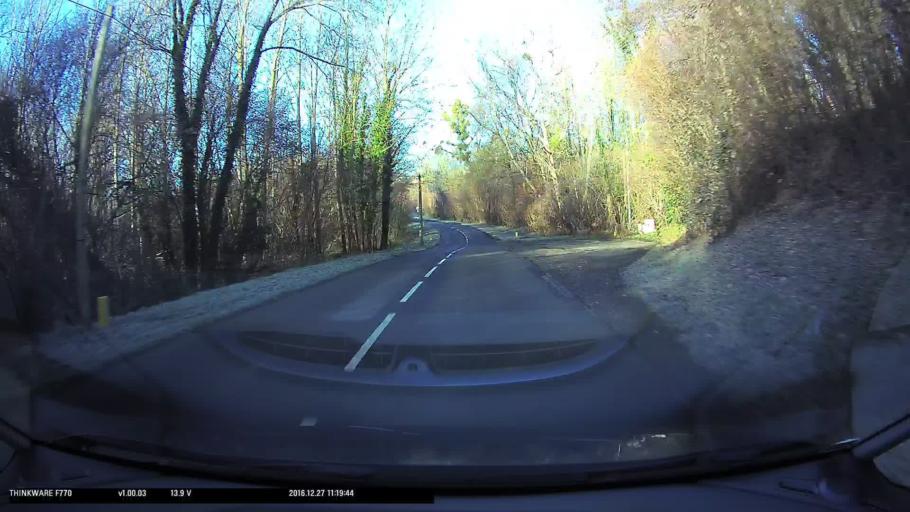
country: FR
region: Ile-de-France
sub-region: Departement du Val-d'Oise
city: Ableiges
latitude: 49.0865
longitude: 1.9945
